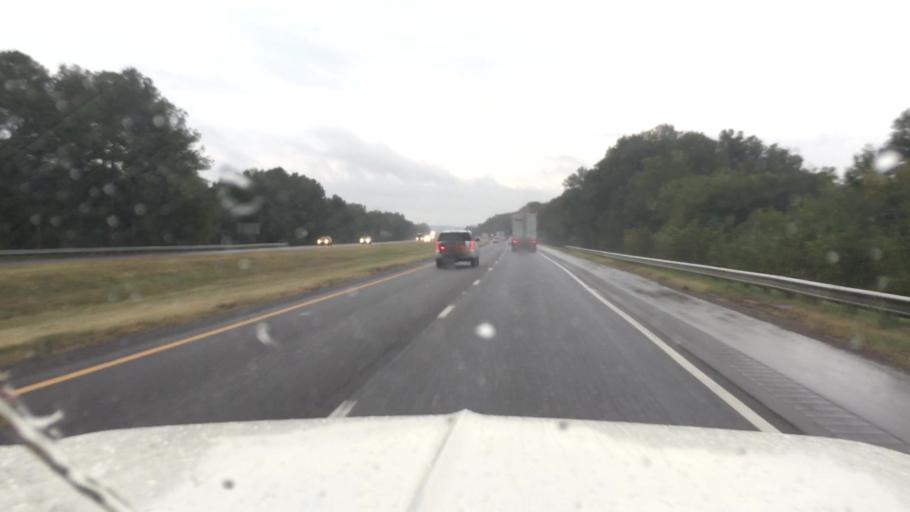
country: US
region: Alabama
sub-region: Morgan County
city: Falkville
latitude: 34.4058
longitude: -86.8982
